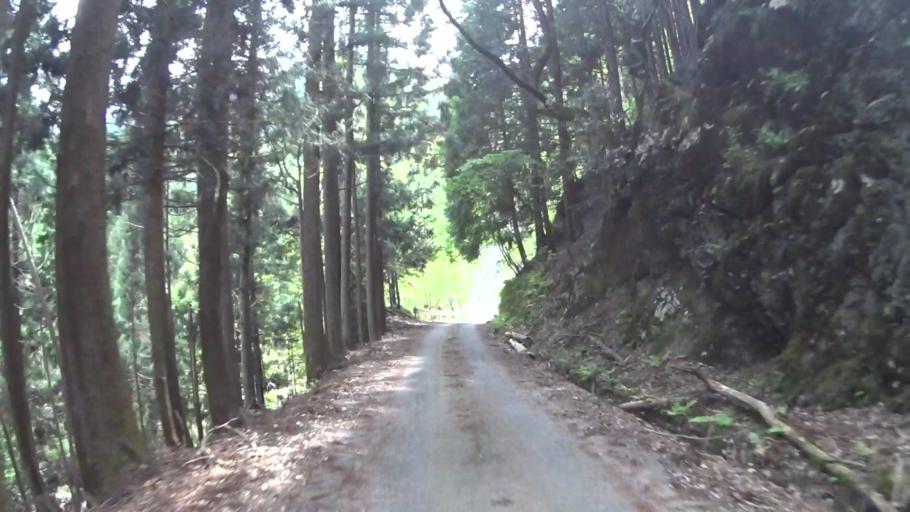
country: JP
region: Kyoto
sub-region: Kyoto-shi
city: Kamigyo-ku
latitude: 35.1933
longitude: 135.7021
